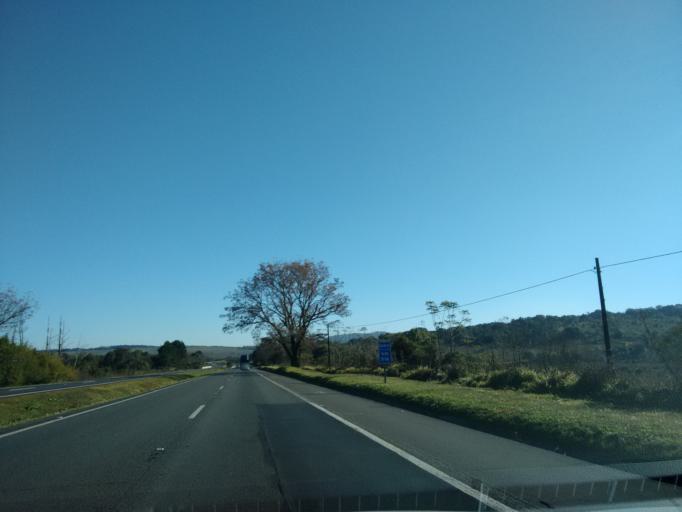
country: BR
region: Parana
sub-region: Palmeira
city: Palmeira
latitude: -25.2540
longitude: -50.0160
